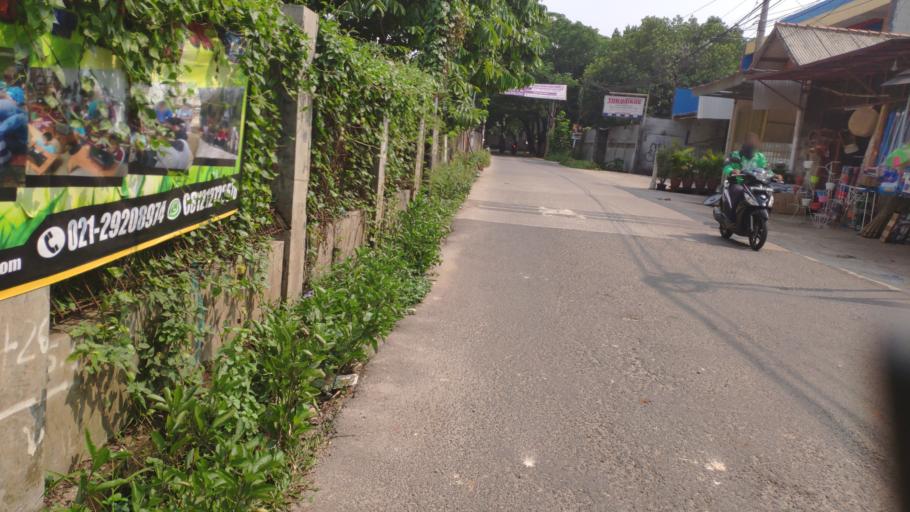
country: ID
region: West Java
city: Depok
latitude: -6.3798
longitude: 106.8017
